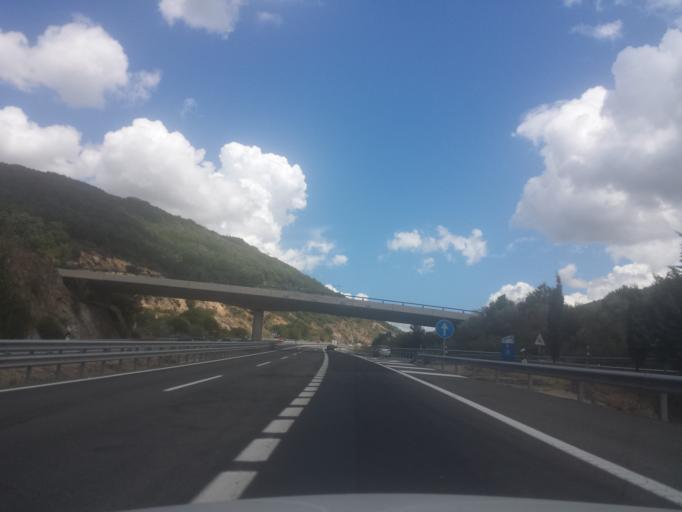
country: ES
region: Extremadura
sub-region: Provincia de Caceres
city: Banos de Montemayor
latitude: 40.3237
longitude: -5.8634
